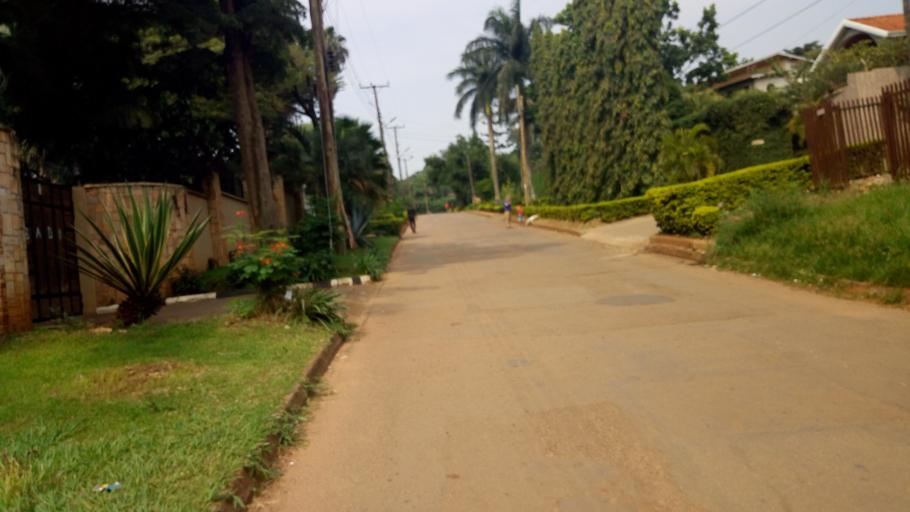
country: UG
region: Central Region
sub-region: Kampala District
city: Kampala
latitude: 0.3175
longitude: 32.6185
